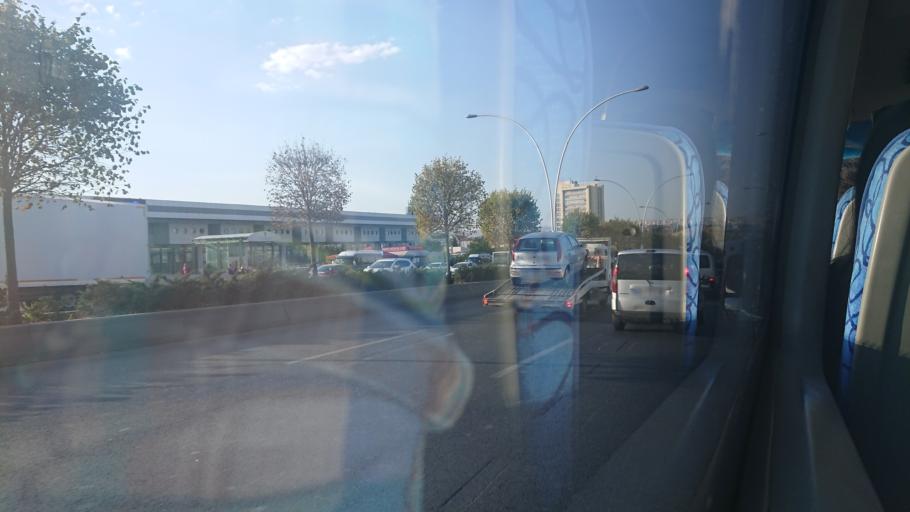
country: TR
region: Ankara
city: Ankara
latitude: 39.9191
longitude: 32.8142
